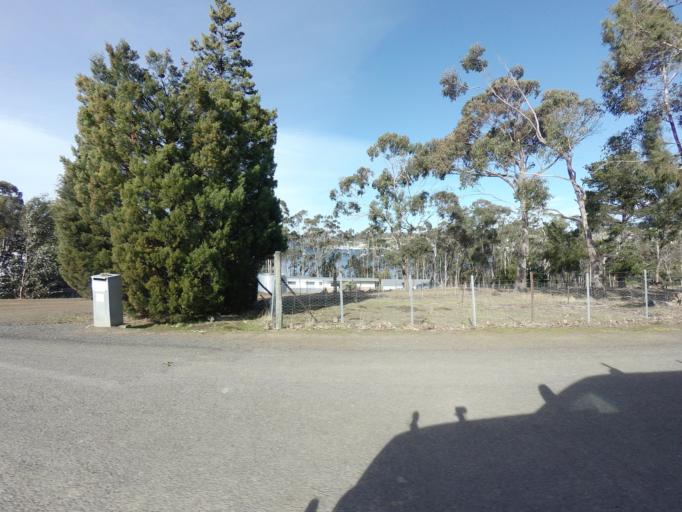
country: AU
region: Tasmania
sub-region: Kingborough
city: Kettering
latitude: -43.1211
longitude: 147.2501
